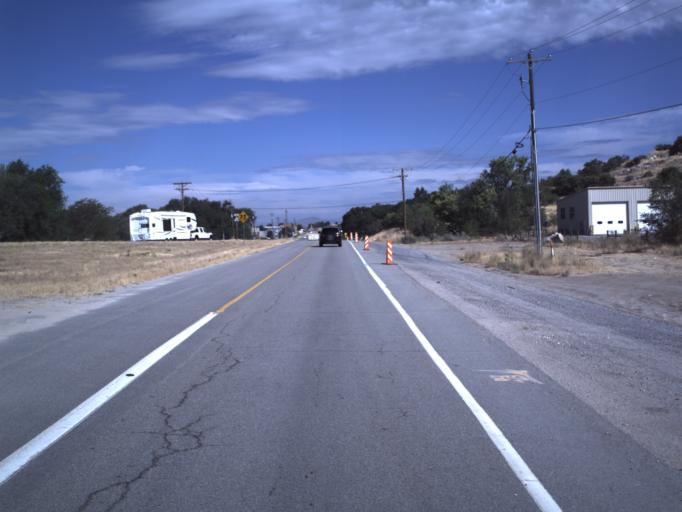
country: US
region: Utah
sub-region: Box Elder County
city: South Willard
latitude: 41.3450
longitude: -112.0327
